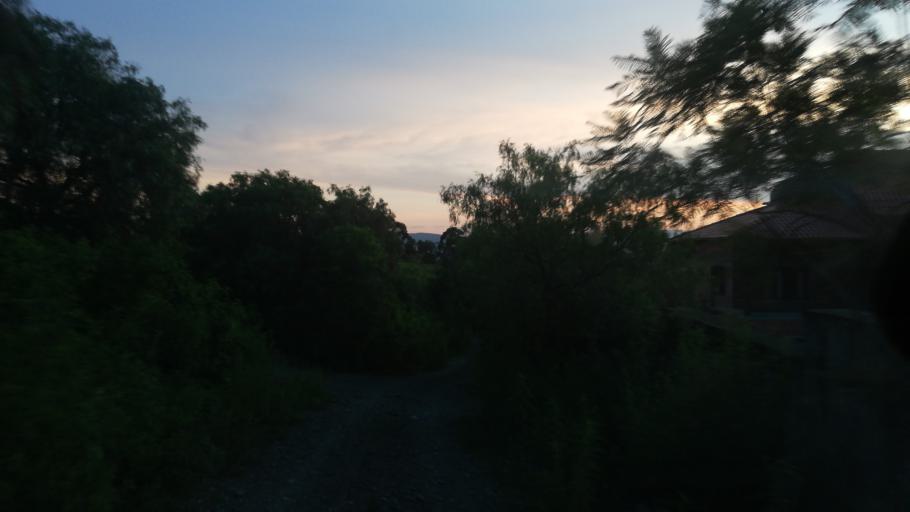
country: BO
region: Cochabamba
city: Cochabamba
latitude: -17.3268
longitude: -66.2070
